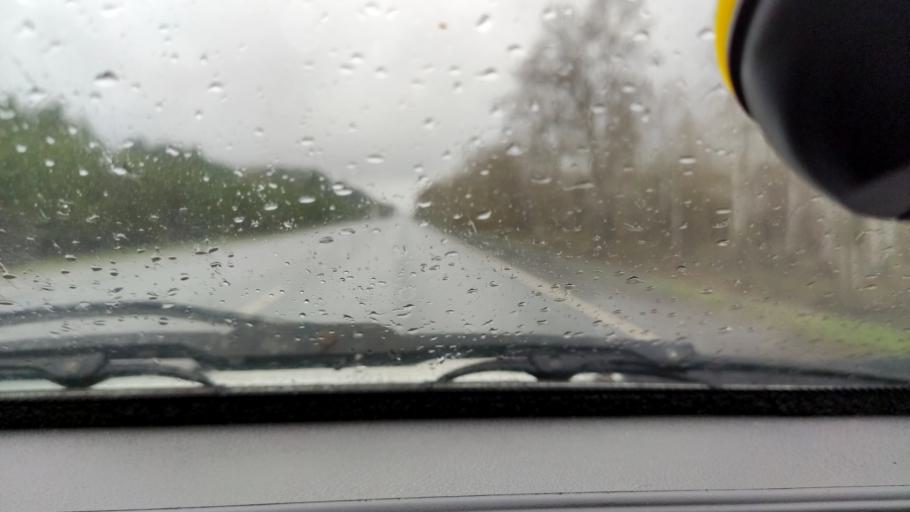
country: RU
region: Samara
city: Povolzhskiy
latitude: 53.6248
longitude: 49.6494
